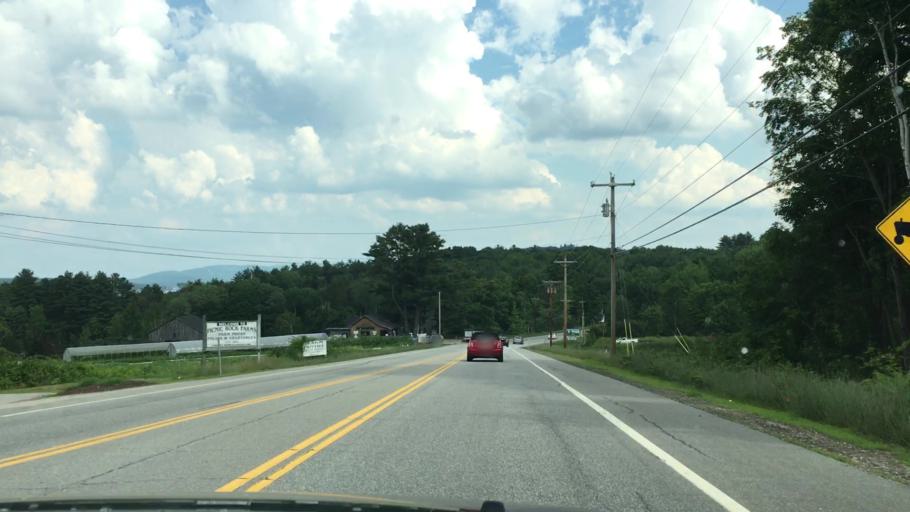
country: US
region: New Hampshire
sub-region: Belknap County
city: Meredith
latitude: 43.6343
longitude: -71.4886
